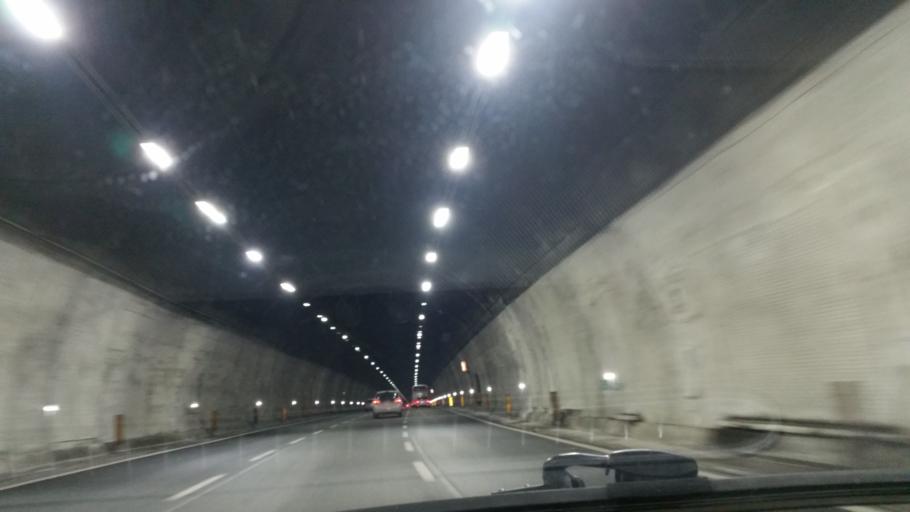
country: IT
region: Campania
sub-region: Provincia di Napoli
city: Napoli
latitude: 40.8571
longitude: 14.2222
